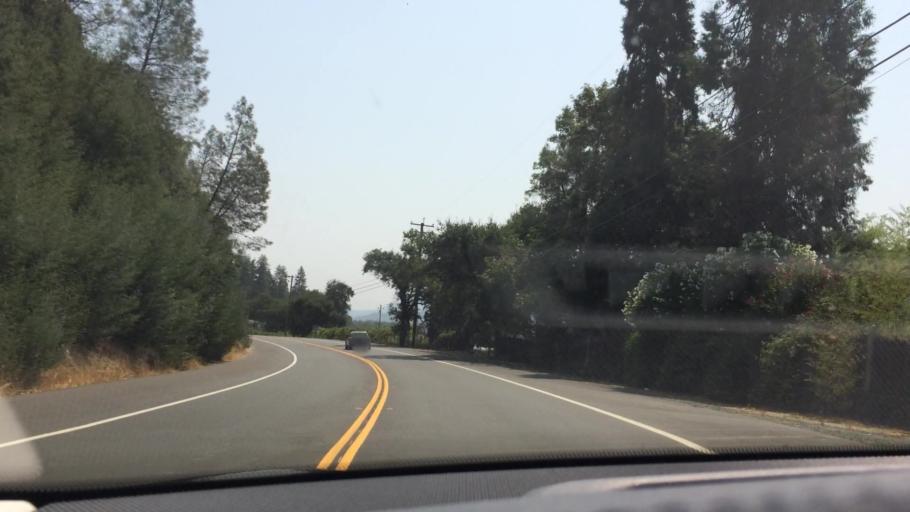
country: US
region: California
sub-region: Napa County
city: Calistoga
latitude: 38.5725
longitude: -122.5183
